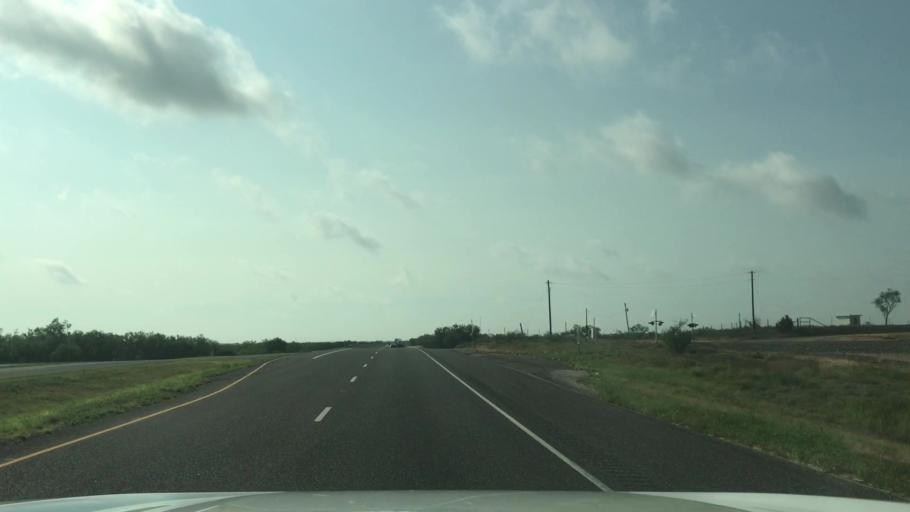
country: US
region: Texas
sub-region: Scurry County
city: Snyder
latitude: 32.8384
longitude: -100.9942
